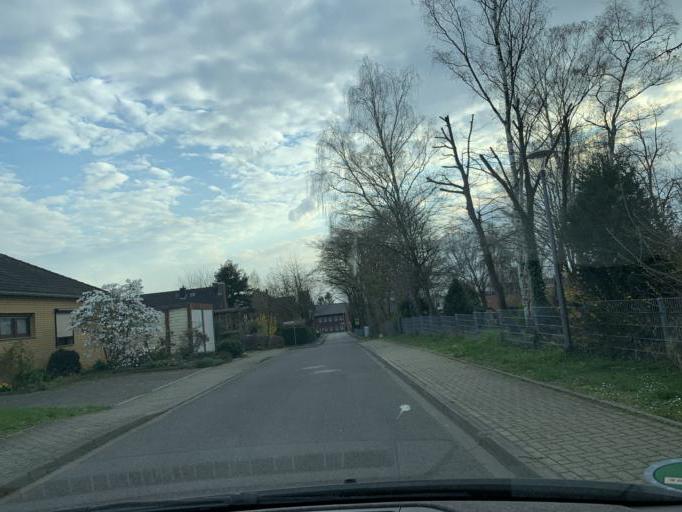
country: DE
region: North Rhine-Westphalia
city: Julich
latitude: 50.9245
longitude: 6.4067
